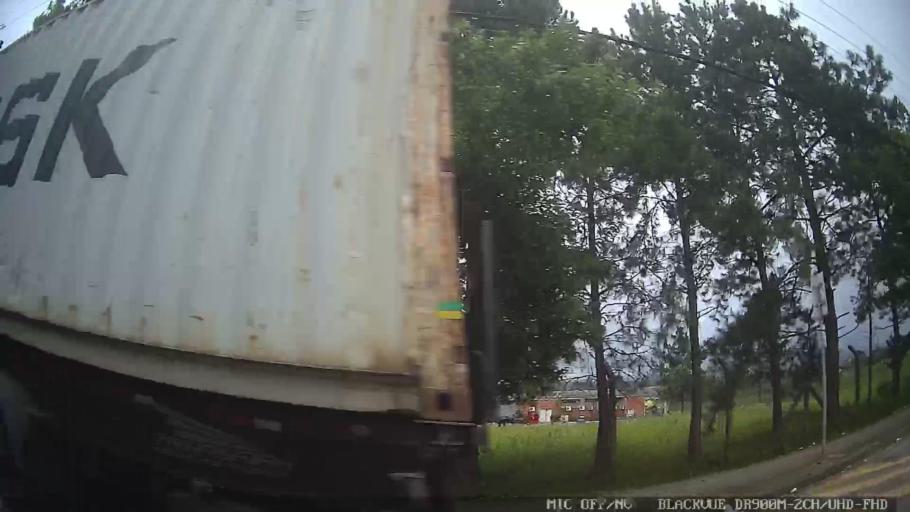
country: BR
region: Sao Paulo
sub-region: Mogi das Cruzes
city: Mogi das Cruzes
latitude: -23.5102
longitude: -46.1559
